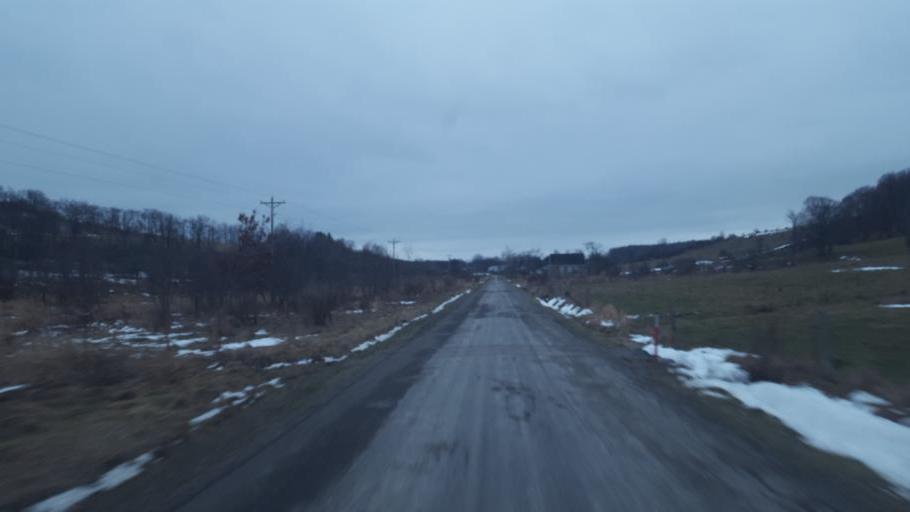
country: US
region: Pennsylvania
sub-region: Potter County
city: Galeton
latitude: 41.8936
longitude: -77.8043
